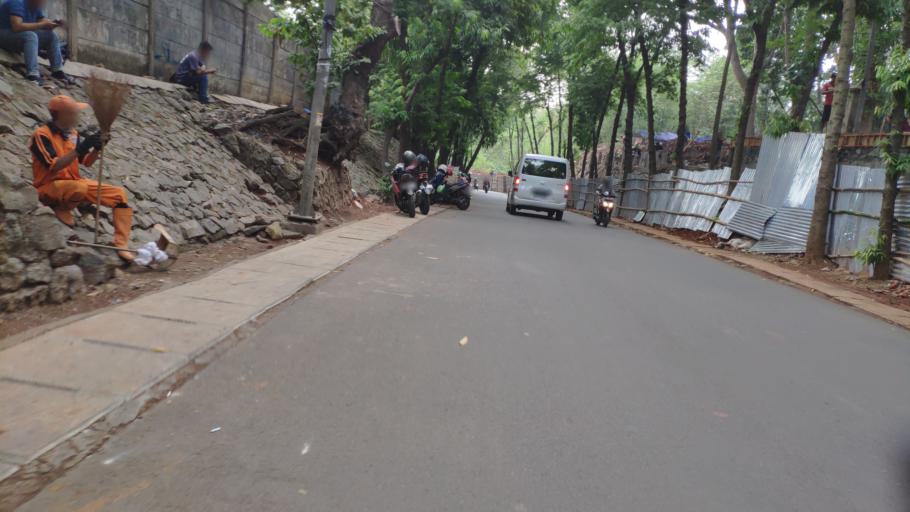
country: ID
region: West Java
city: Pamulang
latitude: -6.3065
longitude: 106.8218
